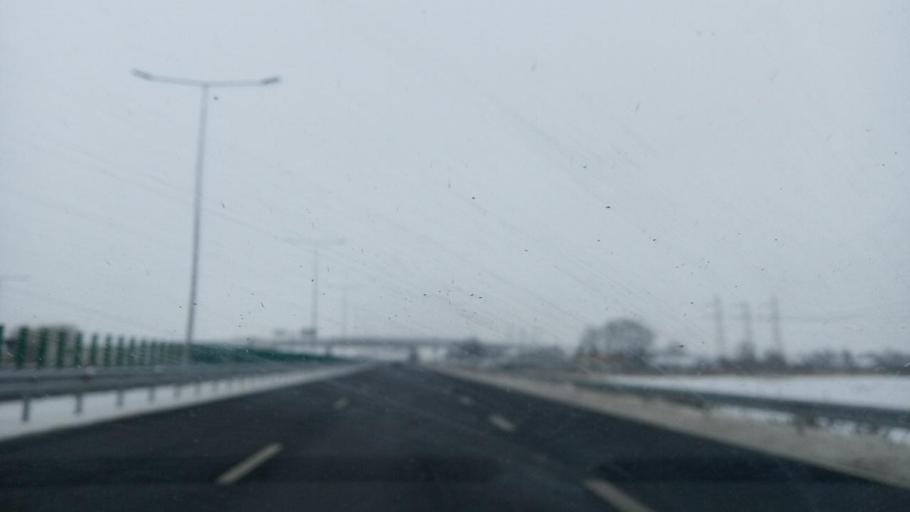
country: RO
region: Bacau
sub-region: Comuna Letea Veche
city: Holt
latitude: 46.5854
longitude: 26.9632
